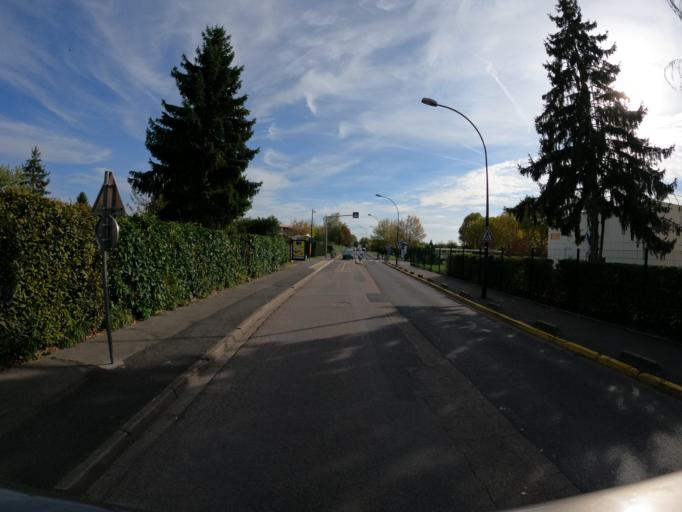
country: FR
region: Ile-de-France
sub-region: Departement de Seine-et-Marne
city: Pontault-Combault
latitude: 48.7881
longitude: 2.5975
